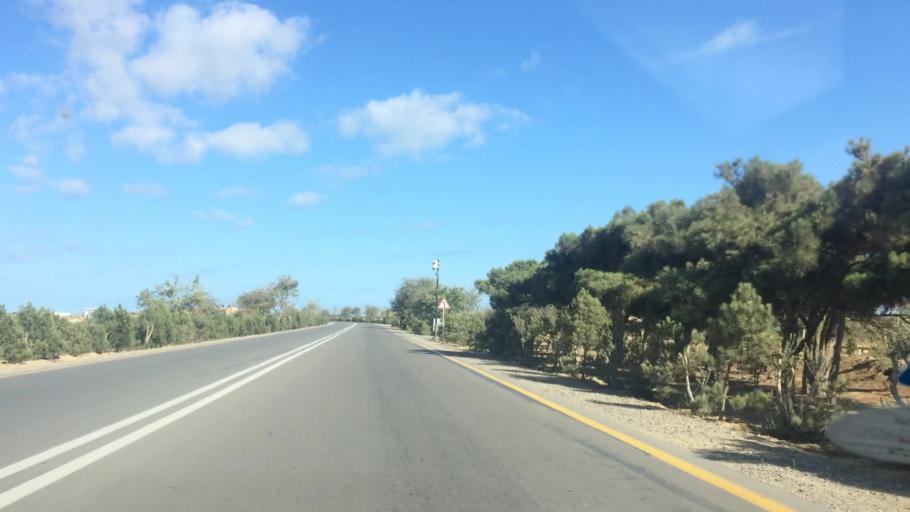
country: AZ
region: Baki
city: Pirallahi
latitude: 40.4202
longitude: 50.3559
